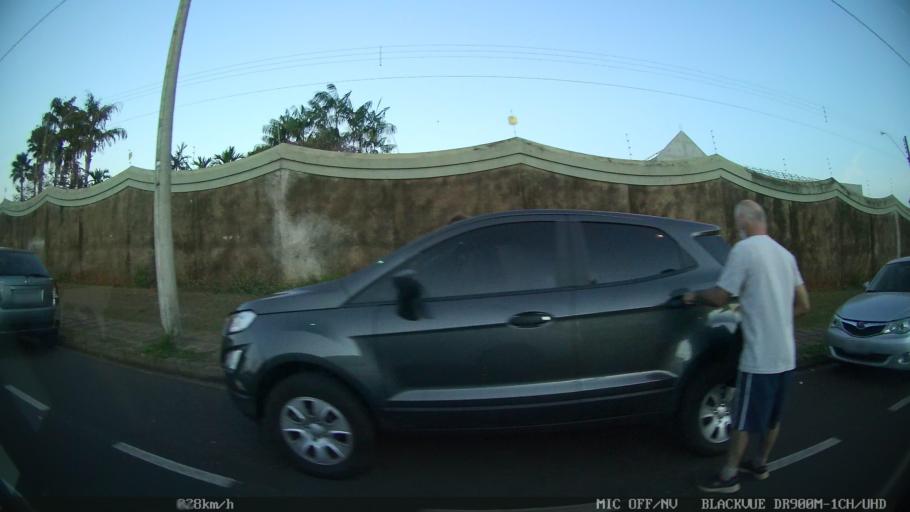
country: BR
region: Sao Paulo
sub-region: Sao Jose Do Rio Preto
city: Sao Jose do Rio Preto
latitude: -20.8099
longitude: -49.3514
